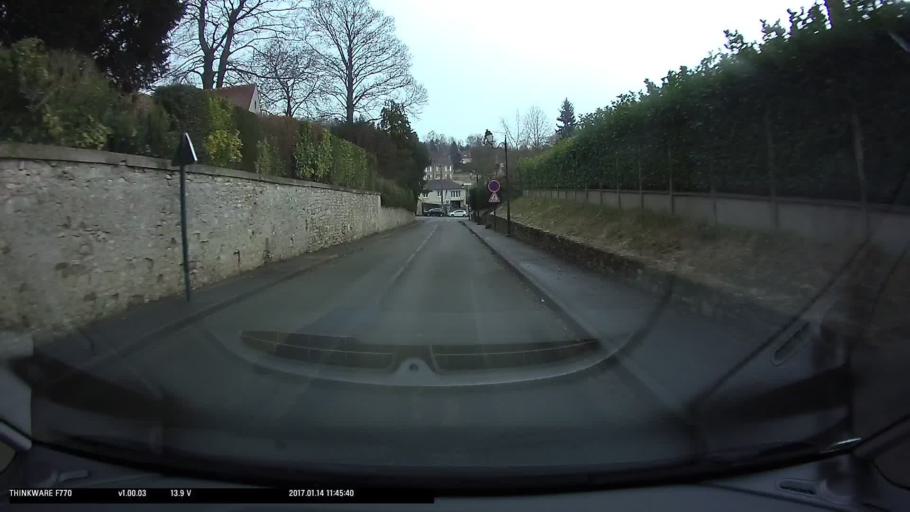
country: FR
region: Ile-de-France
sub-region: Departement du Val-d'Oise
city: Vigny
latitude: 49.0799
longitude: 1.9272
